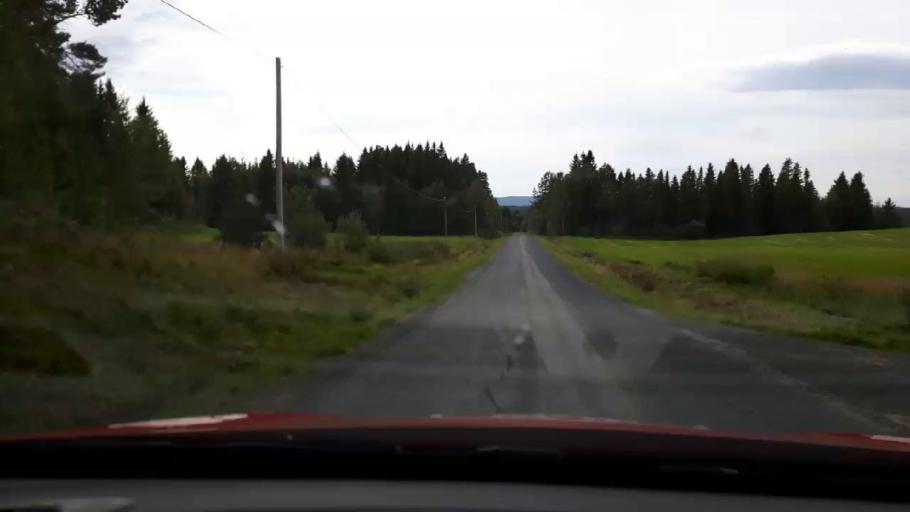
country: SE
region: Jaemtland
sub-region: Krokoms Kommun
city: Valla
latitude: 63.2693
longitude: 13.8544
